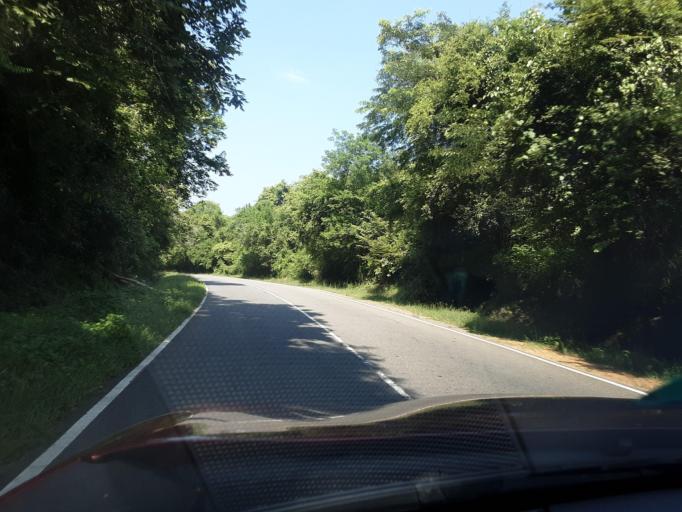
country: LK
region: Uva
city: Badulla
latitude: 7.2723
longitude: 81.0516
